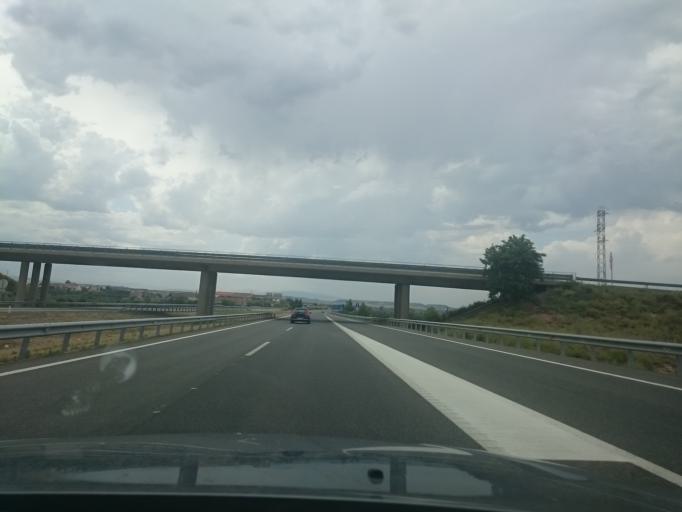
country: ES
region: Navarre
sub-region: Provincia de Navarra
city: Murchante
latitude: 42.0321
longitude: -1.6353
